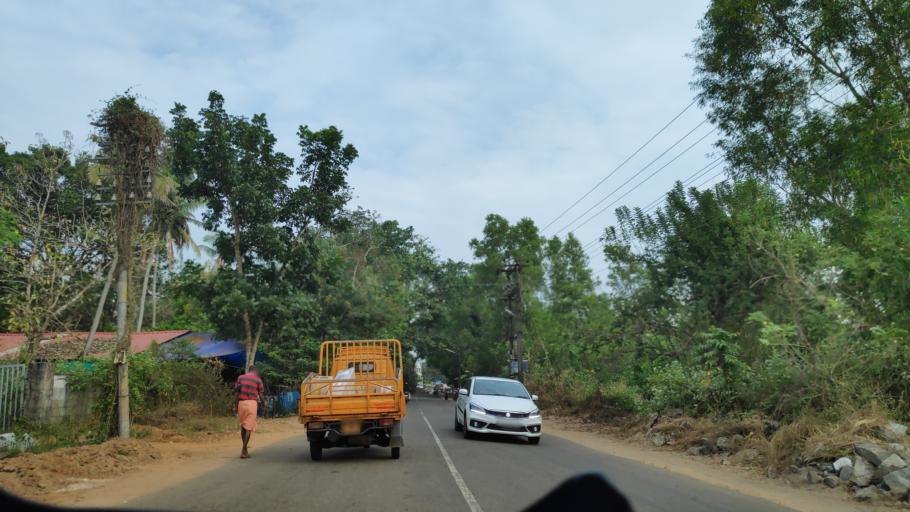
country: IN
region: Kerala
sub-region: Alappuzha
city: Vayalar
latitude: 9.7231
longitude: 76.3608
